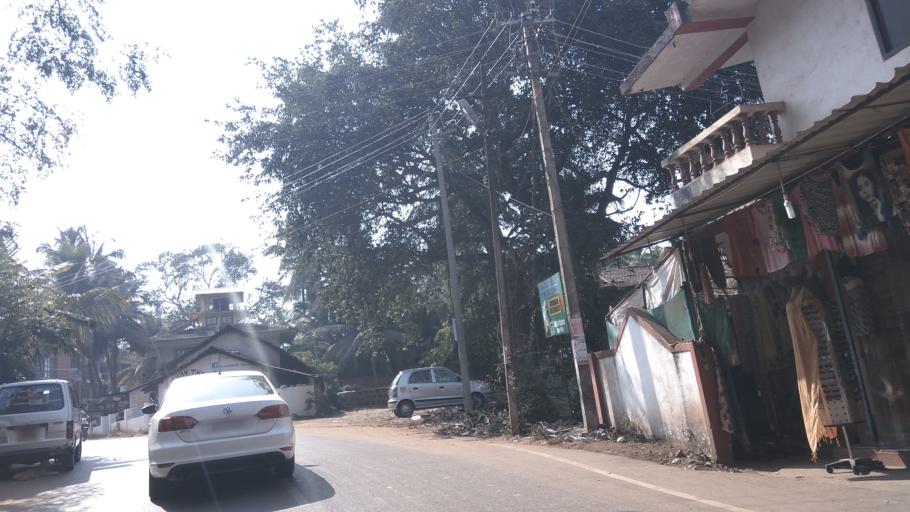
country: IN
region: Goa
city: Calangute
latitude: 15.5562
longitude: 73.7580
